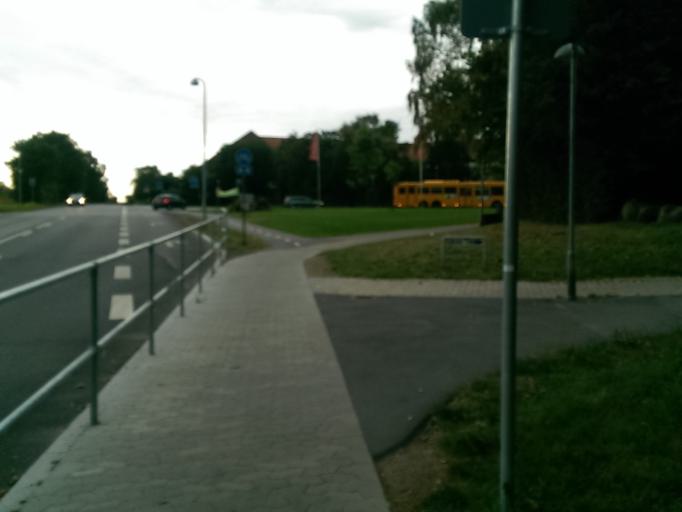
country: DK
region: Zealand
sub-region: Roskilde Kommune
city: Viby
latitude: 55.5509
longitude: 12.0261
